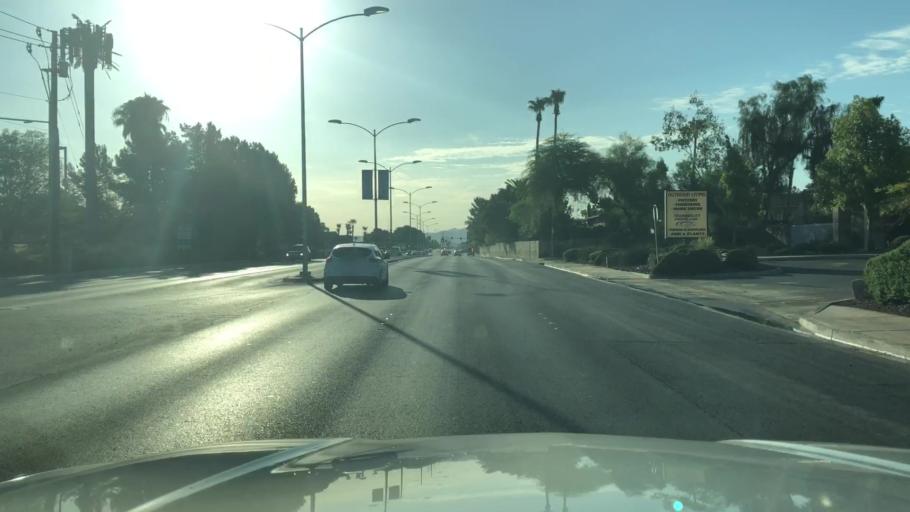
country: US
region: Nevada
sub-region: Clark County
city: Whitney
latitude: 36.0636
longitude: -115.0560
